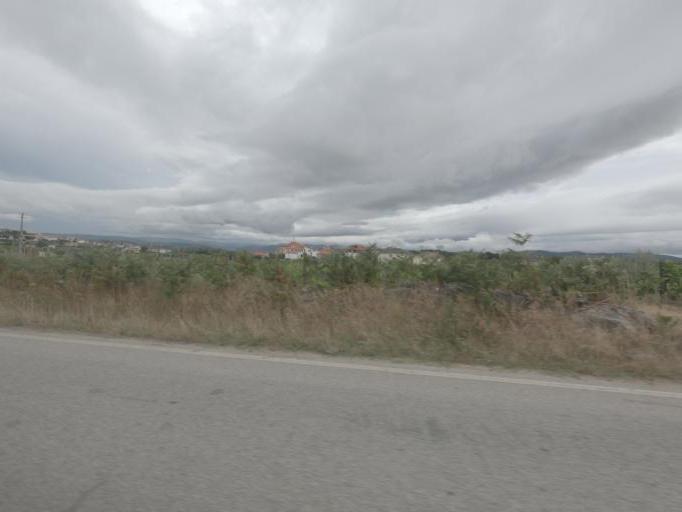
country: PT
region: Vila Real
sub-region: Sabrosa
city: Sabrosa
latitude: 41.2763
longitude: -7.5094
